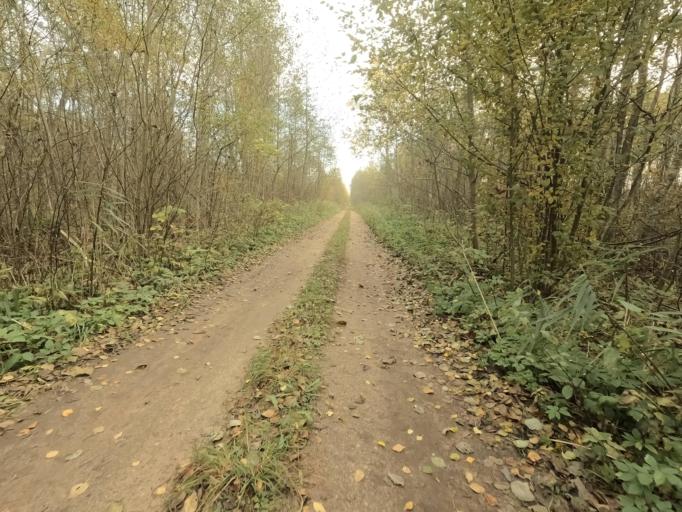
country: RU
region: Novgorod
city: Pankovka
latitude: 58.8797
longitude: 30.8511
